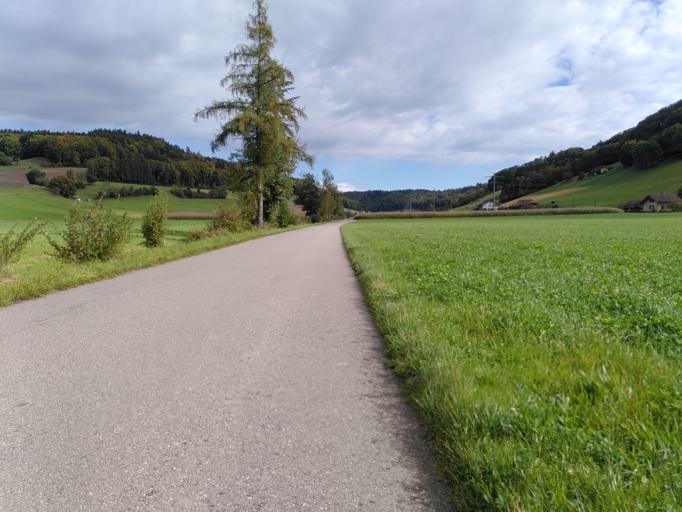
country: CH
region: Bern
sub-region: Oberaargau
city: Seeberg
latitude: 47.1296
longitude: 7.6775
